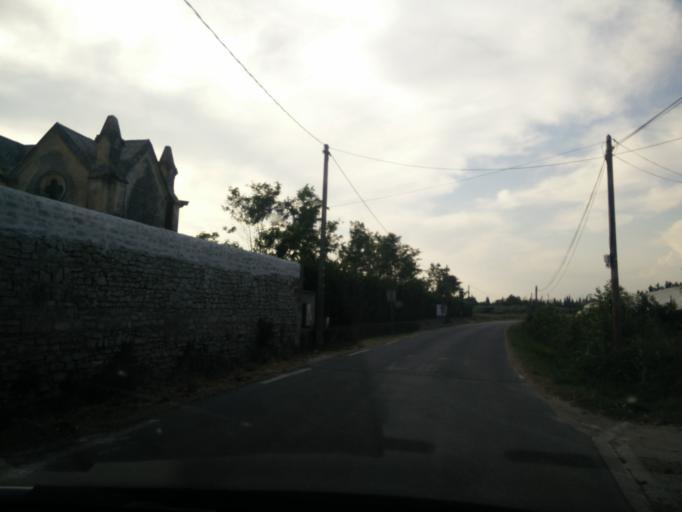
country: FR
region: Languedoc-Roussillon
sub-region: Departement de l'Herault
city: Marsillargues
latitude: 43.6720
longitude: 4.1749
